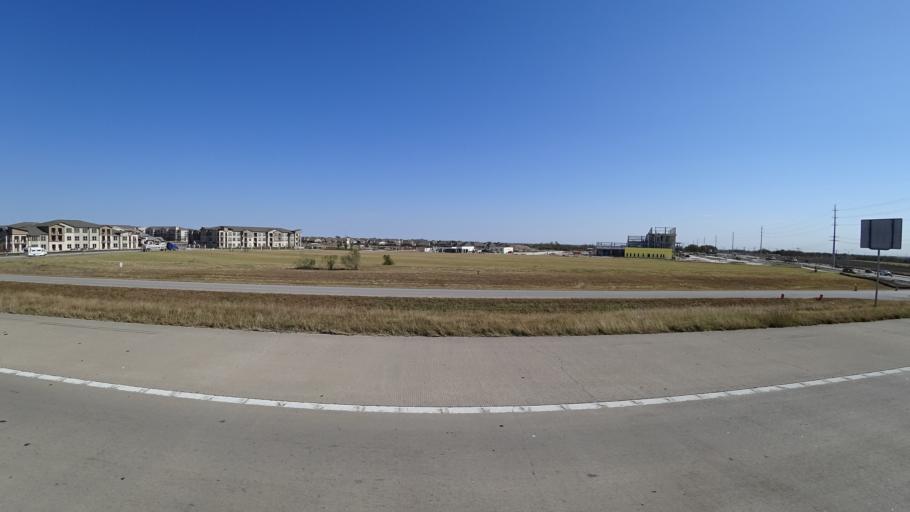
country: US
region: Texas
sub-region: Travis County
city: Pflugerville
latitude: 30.4527
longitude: -97.5940
